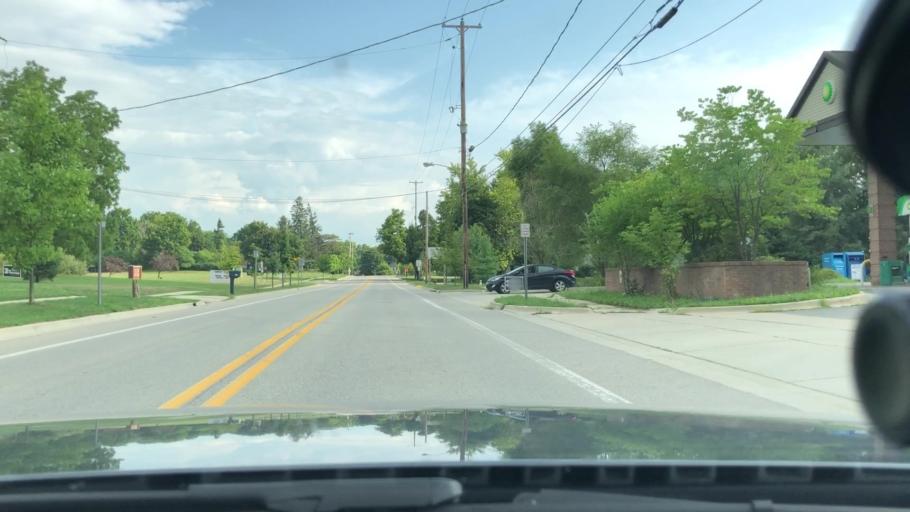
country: US
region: Michigan
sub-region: Washtenaw County
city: Manchester
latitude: 42.1562
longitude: -84.0411
